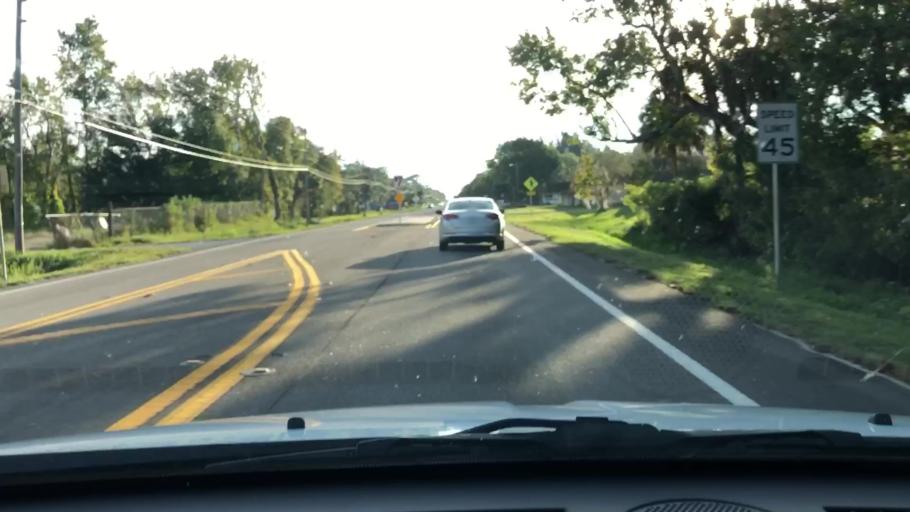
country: US
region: Florida
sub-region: Osceola County
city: Campbell
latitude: 28.2615
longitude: -81.5126
